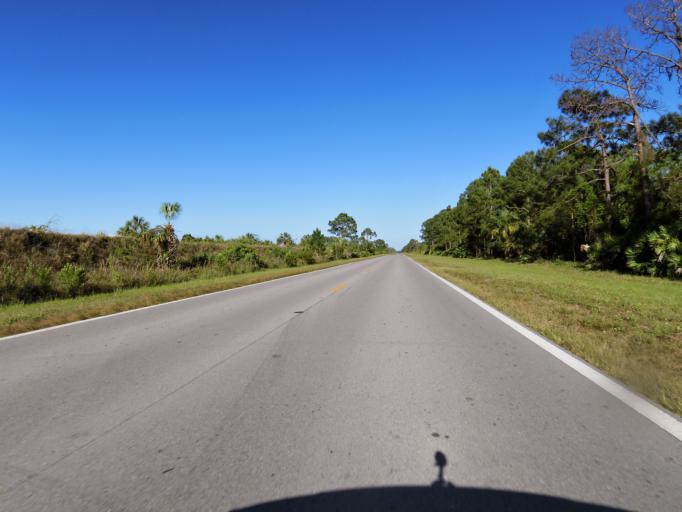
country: US
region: Florida
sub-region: Collier County
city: Immokalee
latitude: 26.2950
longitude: -81.4080
